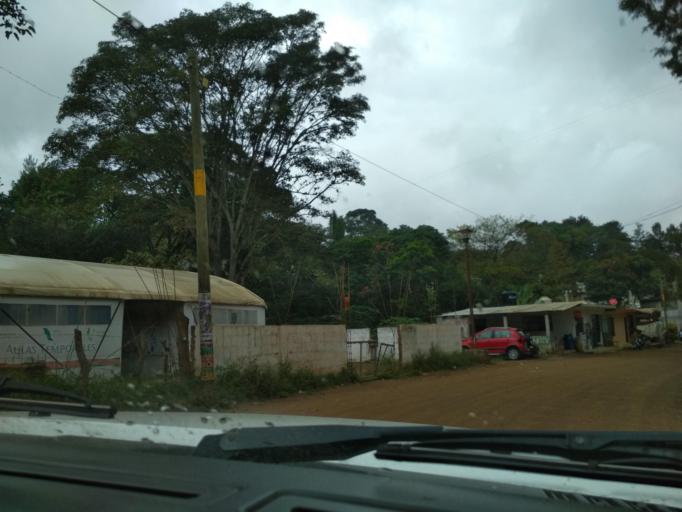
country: MX
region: Veracruz
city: El Castillo
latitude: 19.5439
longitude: -96.8338
